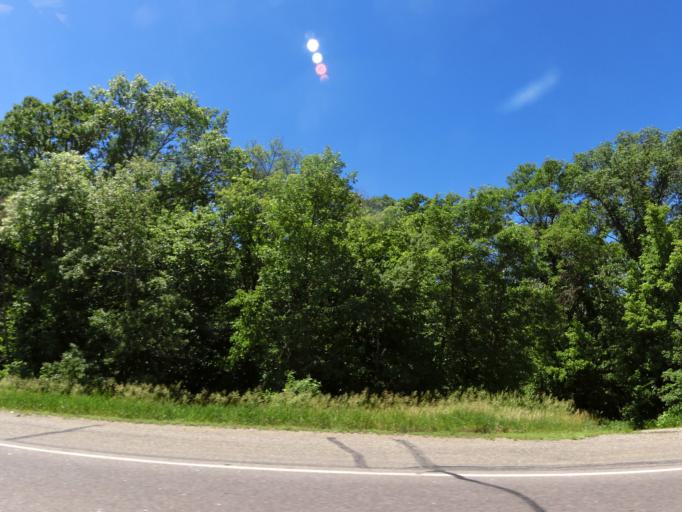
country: US
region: Minnesota
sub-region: Becker County
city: Detroit Lakes
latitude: 46.7932
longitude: -95.8065
